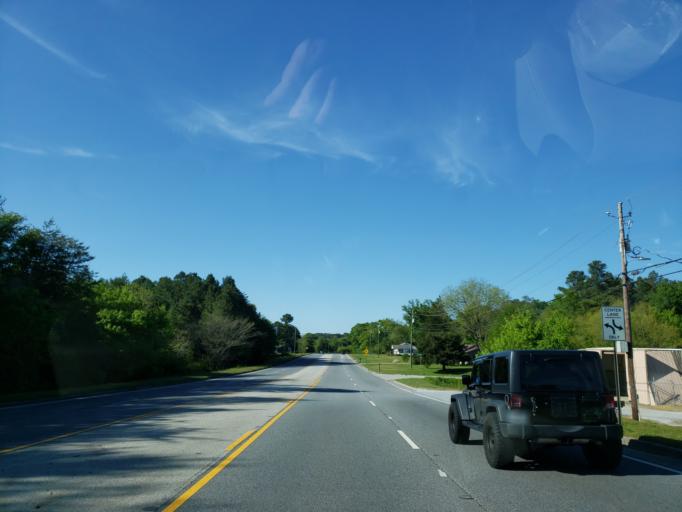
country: US
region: Georgia
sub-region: Polk County
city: Cedartown
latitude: 33.9751
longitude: -85.2580
